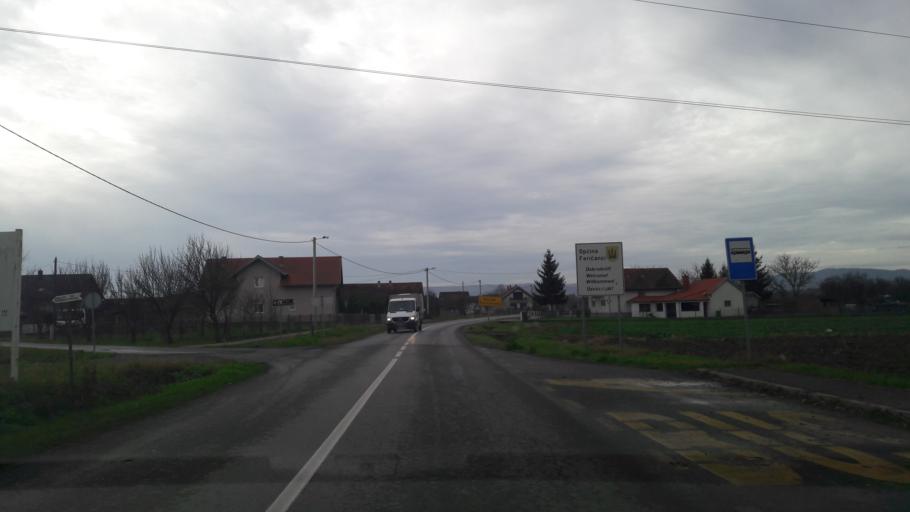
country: HR
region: Osjecko-Baranjska
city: Martin
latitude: 45.5314
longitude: 18.0317
